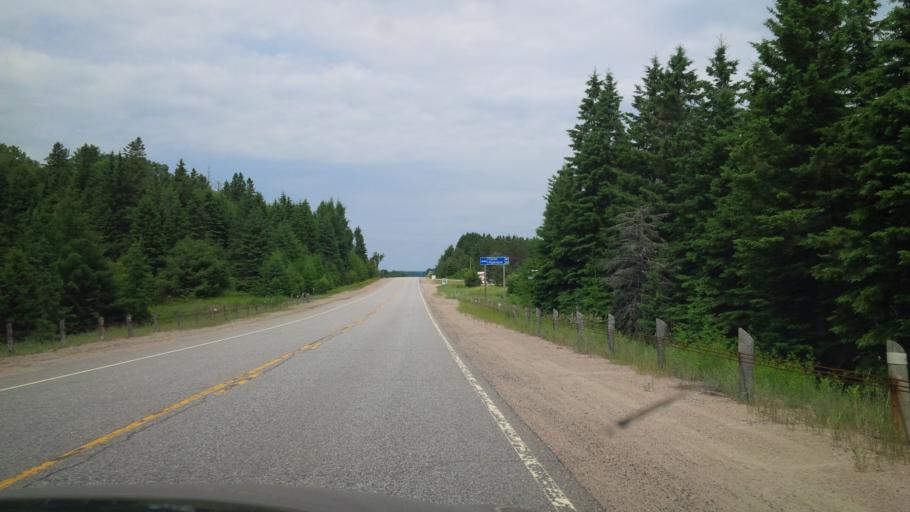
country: CA
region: Ontario
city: Huntsville
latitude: 45.5212
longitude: -79.3148
